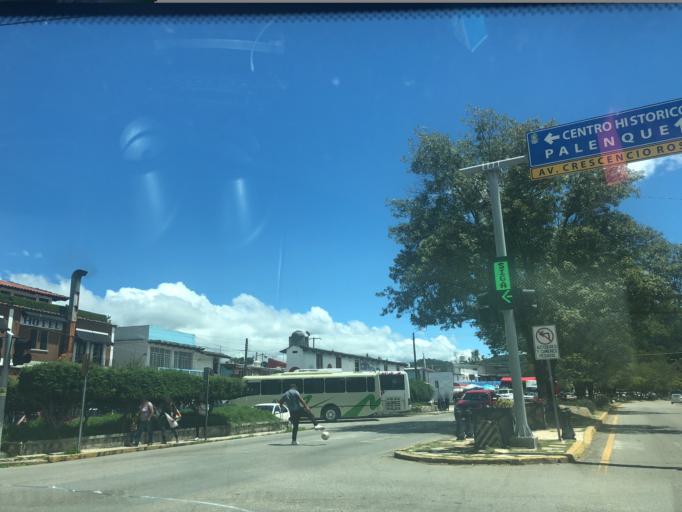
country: MX
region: Chiapas
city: San Cristobal de las Casas
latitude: 16.7302
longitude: -92.6392
